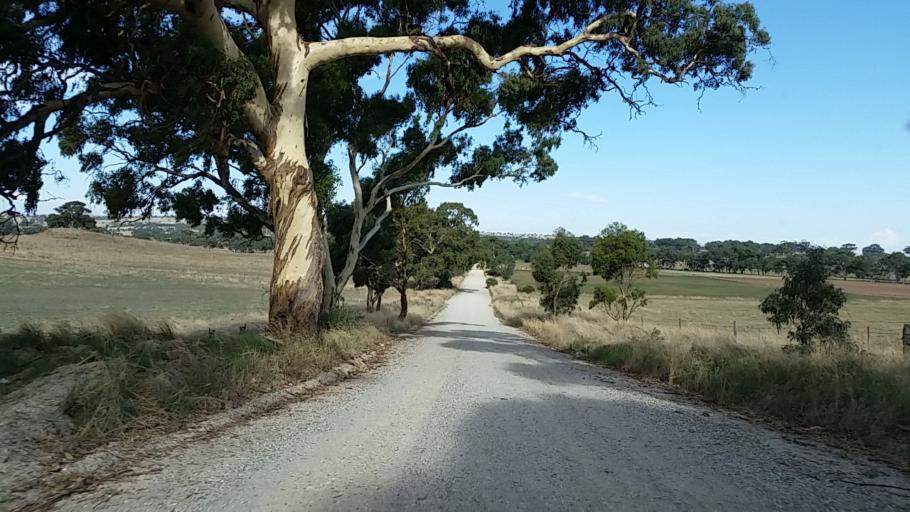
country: AU
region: South Australia
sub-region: Barossa
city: Angaston
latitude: -34.5794
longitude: 139.1418
